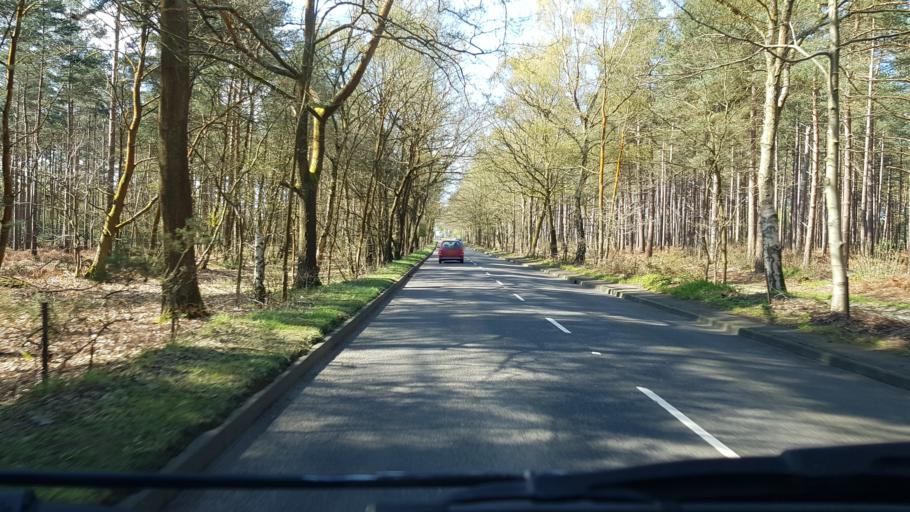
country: GB
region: England
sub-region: Surrey
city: Pirbright
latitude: 51.2718
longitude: -0.6572
